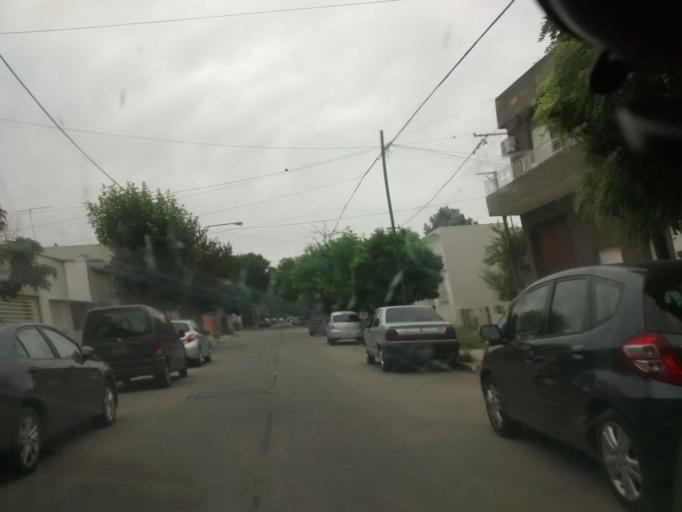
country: AR
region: Buenos Aires
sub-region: Partido de La Plata
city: La Plata
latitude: -34.9311
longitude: -57.9382
